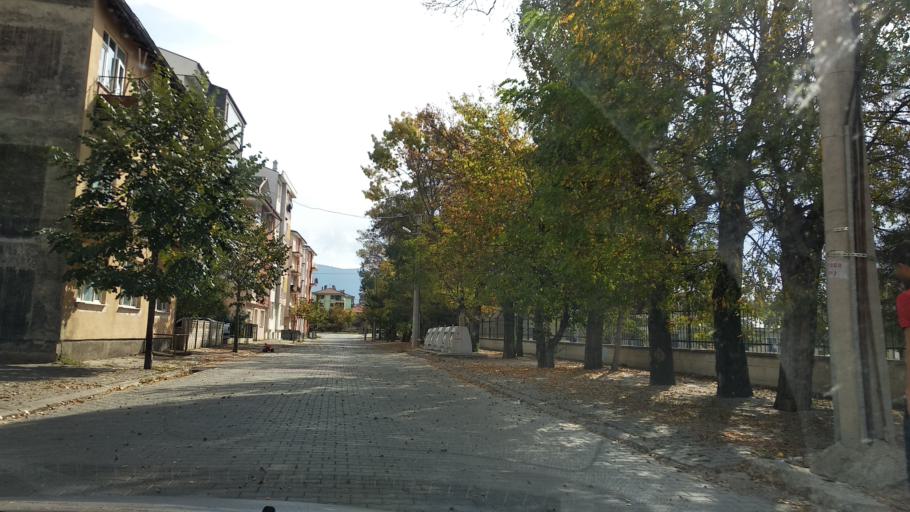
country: TR
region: Bolu
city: Bolu
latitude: 40.7399
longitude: 31.6041
